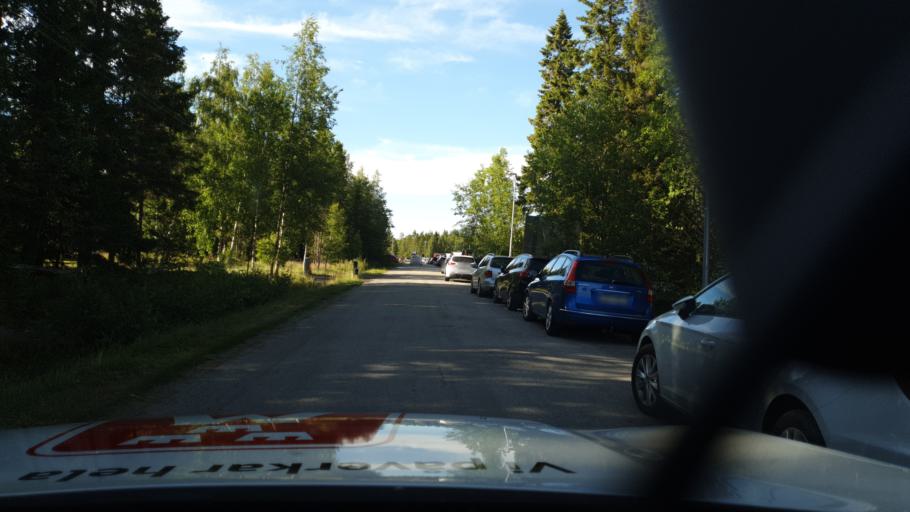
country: SE
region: Vaesterbotten
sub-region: Umea Kommun
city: Saevar
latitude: 63.8629
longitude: 20.7374
